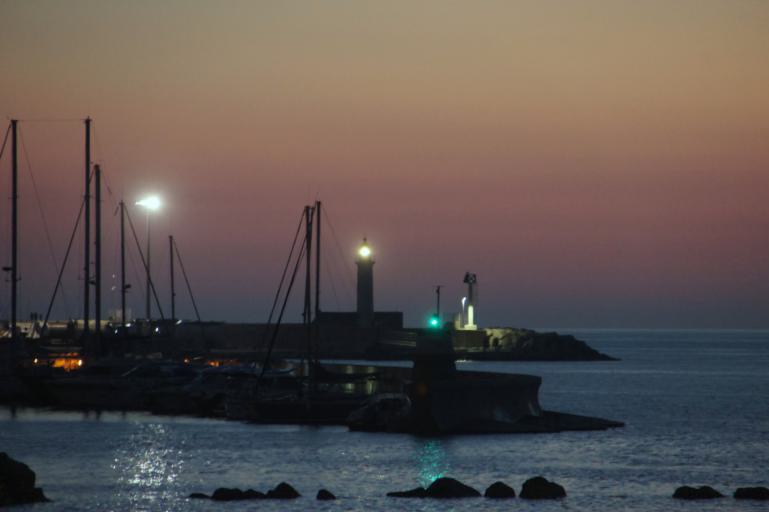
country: FR
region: Corsica
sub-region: Departement de la Corse-du-Sud
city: Propriano
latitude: 41.6775
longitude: 8.9099
